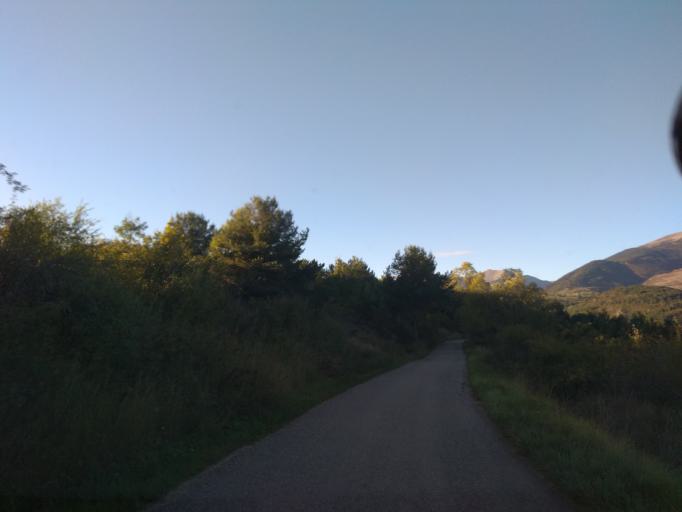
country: ES
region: Catalonia
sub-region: Provincia de Lleida
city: Lles de Cerdanya
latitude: 42.3565
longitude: 1.7244
